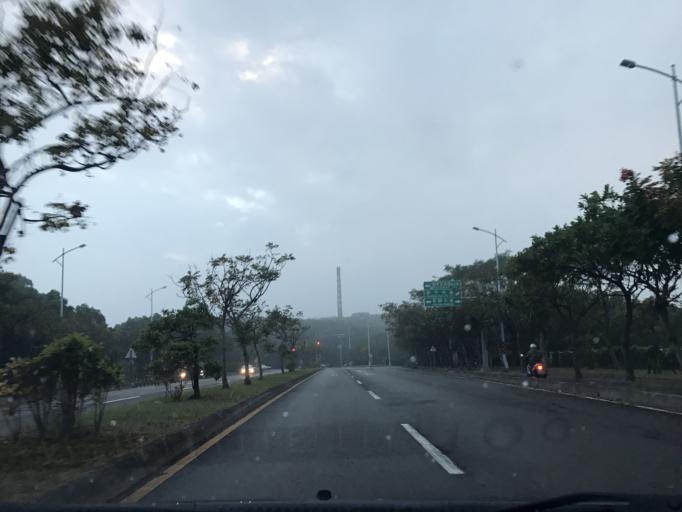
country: TW
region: Taiwan
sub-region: Hsinchu
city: Hsinchu
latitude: 24.7842
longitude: 120.9554
